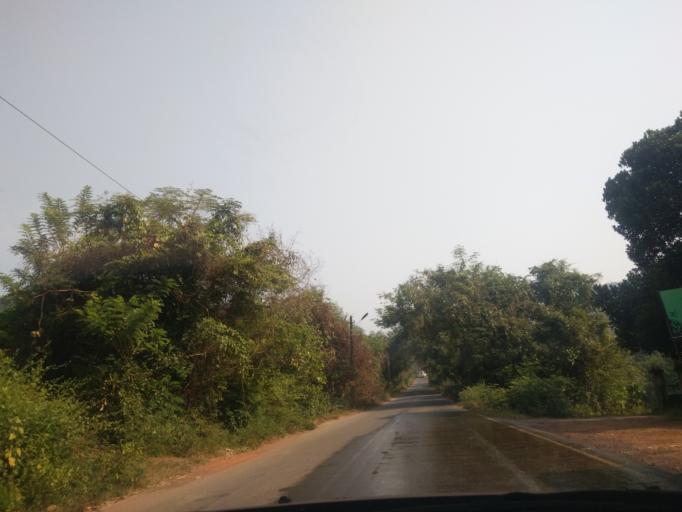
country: IN
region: Goa
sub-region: North Goa
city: Palle
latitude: 15.4499
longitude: 74.0677
